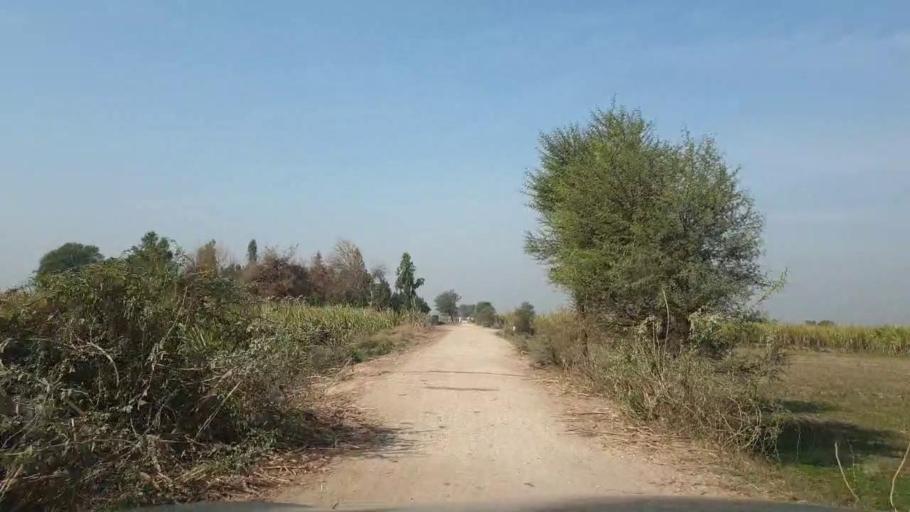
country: PK
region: Sindh
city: Tando Allahyar
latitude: 25.6023
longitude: 68.7171
